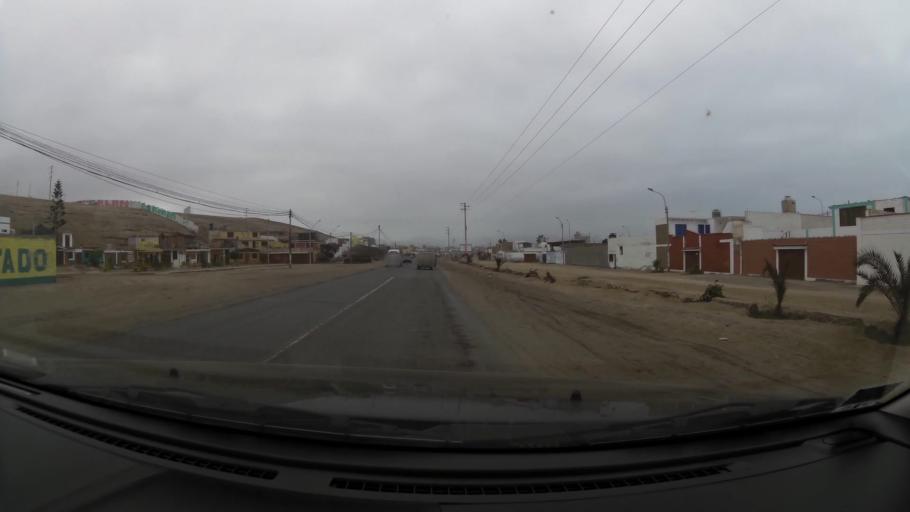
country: PE
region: Lima
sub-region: Lima
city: Punta Hermosa
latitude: -12.3576
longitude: -76.8017
